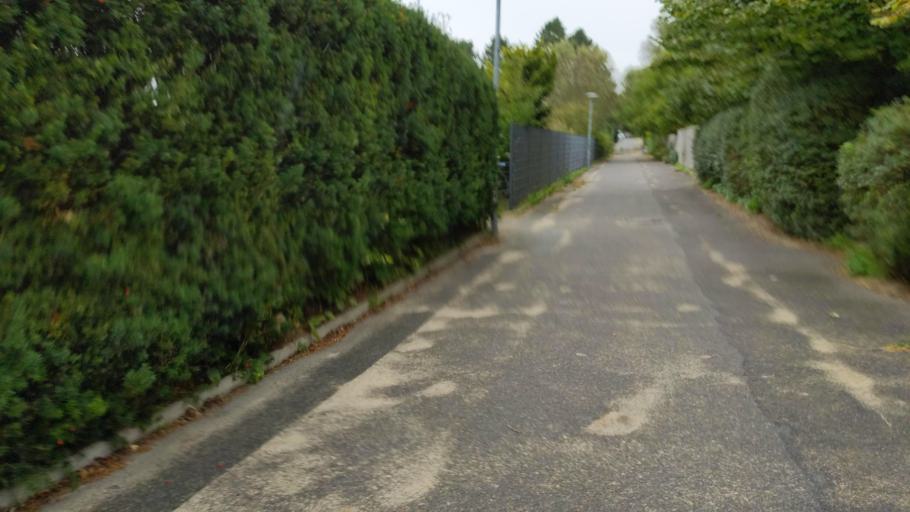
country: DE
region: Schleswig-Holstein
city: Gross Gronau
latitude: 53.8443
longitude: 10.7384
